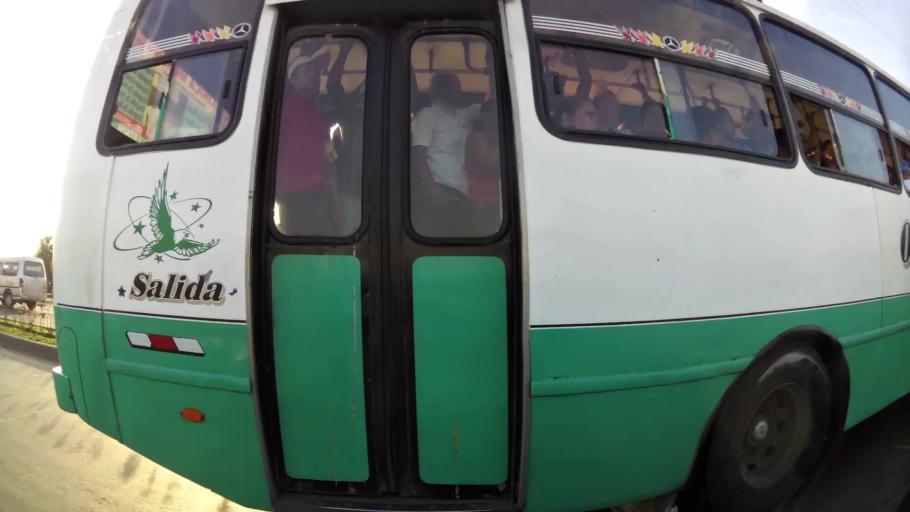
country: EC
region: Guayas
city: Eloy Alfaro
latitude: -2.1486
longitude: -79.8765
